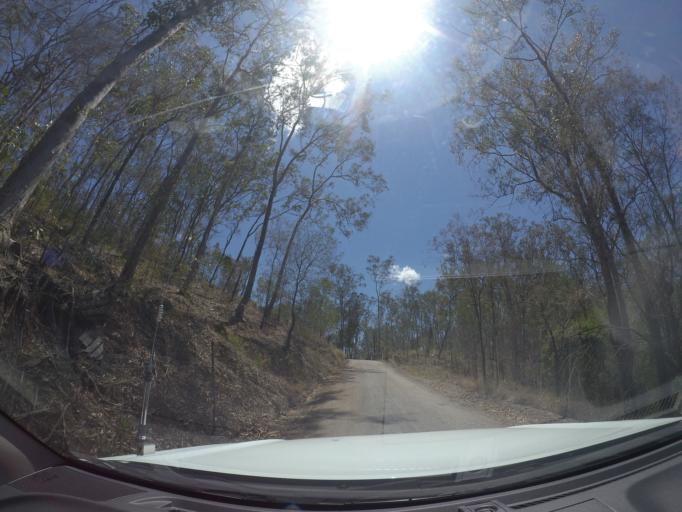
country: AU
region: Queensland
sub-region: Ipswich
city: Springfield Lakes
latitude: -27.8054
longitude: 152.8438
